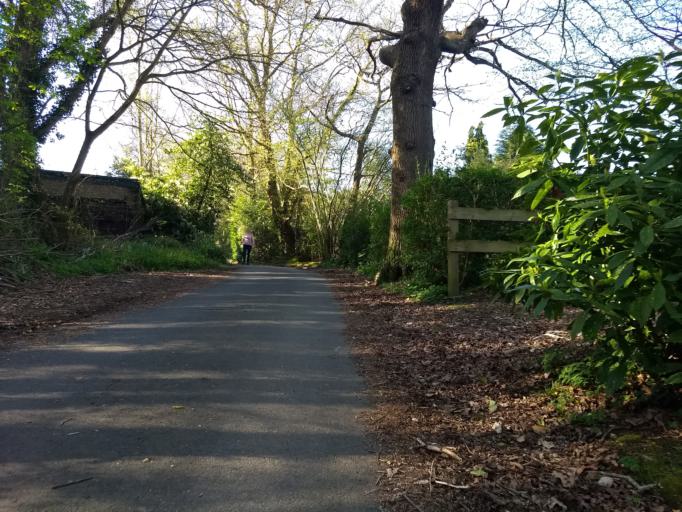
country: GB
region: England
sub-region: Isle of Wight
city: Ryde
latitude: 50.7276
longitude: -1.2191
